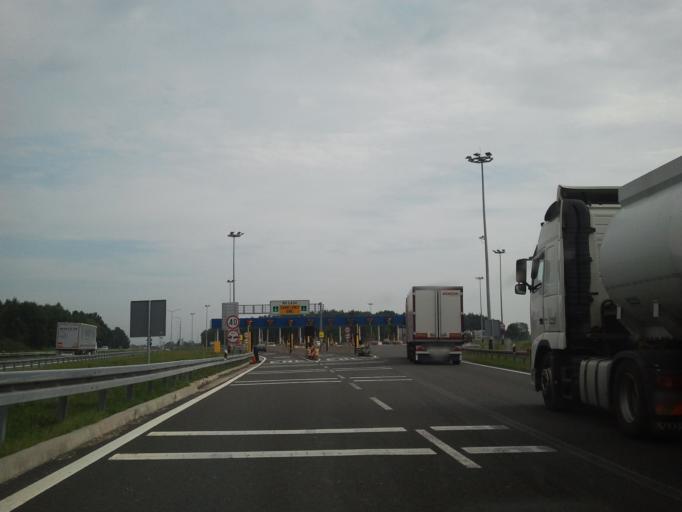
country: HR
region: Grad Zagreb
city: Brezovica
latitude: 45.7221
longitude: 15.8684
